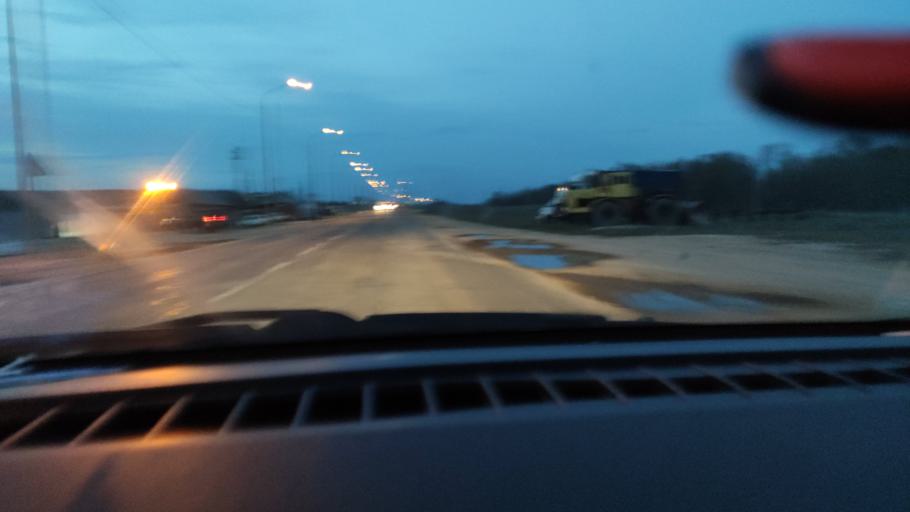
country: RU
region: Saratov
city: Sinodskoye
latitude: 52.0865
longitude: 46.8029
